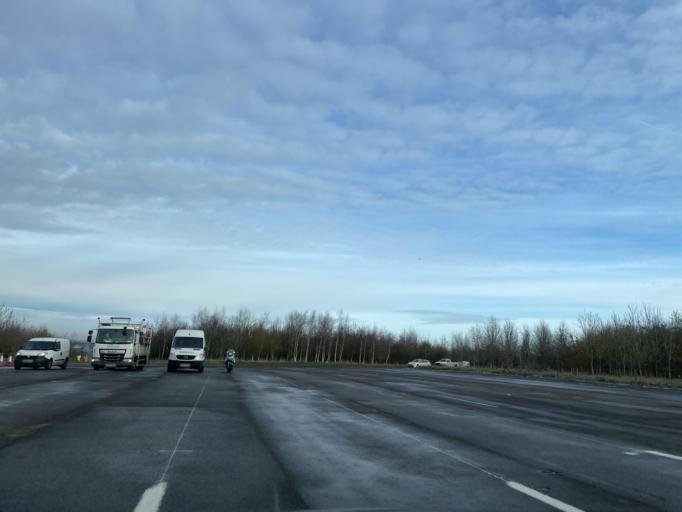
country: GB
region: England
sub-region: Borough of Swindon
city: Wroughton
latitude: 51.5144
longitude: -1.7949
